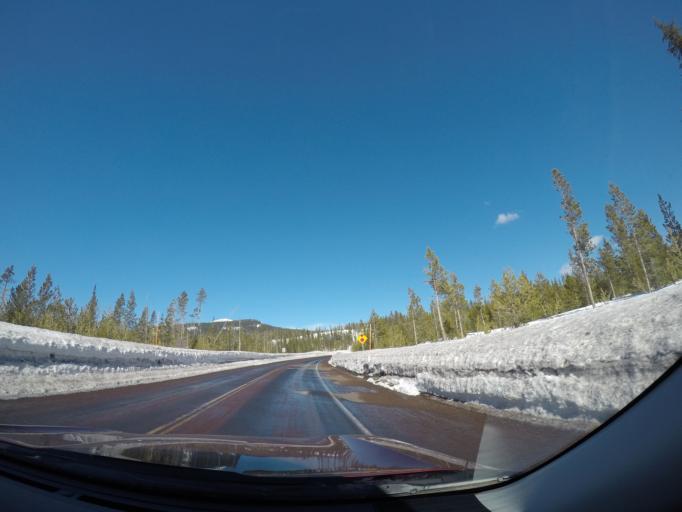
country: US
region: Oregon
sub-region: Deschutes County
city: Sunriver
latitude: 43.9801
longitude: -121.6128
